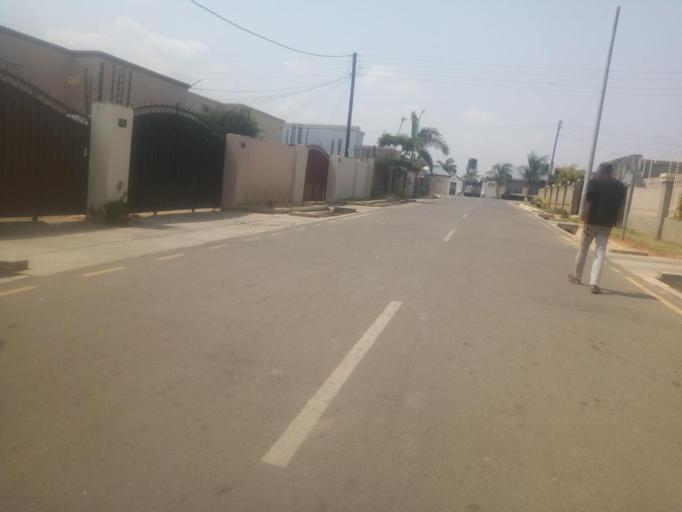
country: ZM
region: Lusaka
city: Lusaka
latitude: -15.3966
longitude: 28.3914
